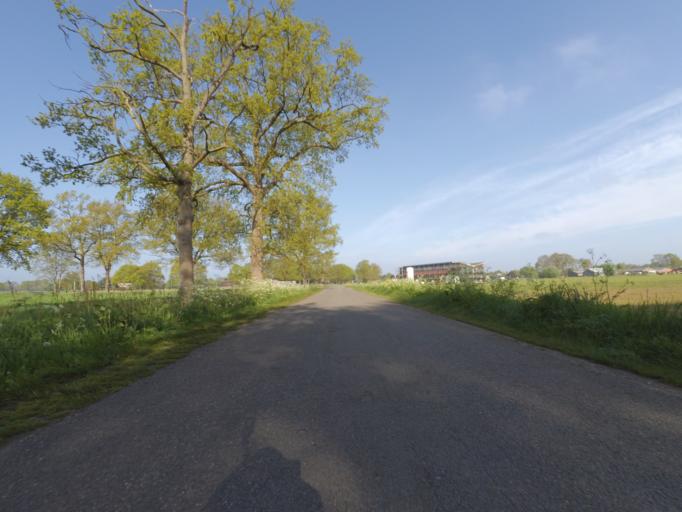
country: NL
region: Gelderland
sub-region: Gemeente Barneveld
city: Voorthuizen
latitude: 52.1733
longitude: 5.5990
